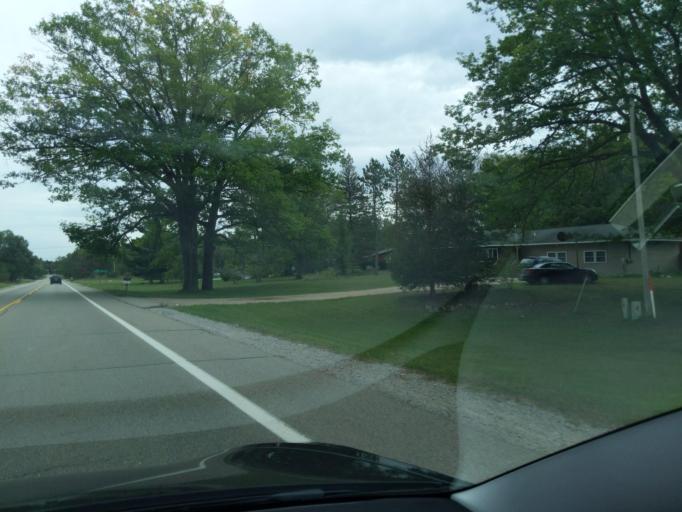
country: US
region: Michigan
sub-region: Clare County
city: Clare
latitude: 43.8459
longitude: -84.8887
